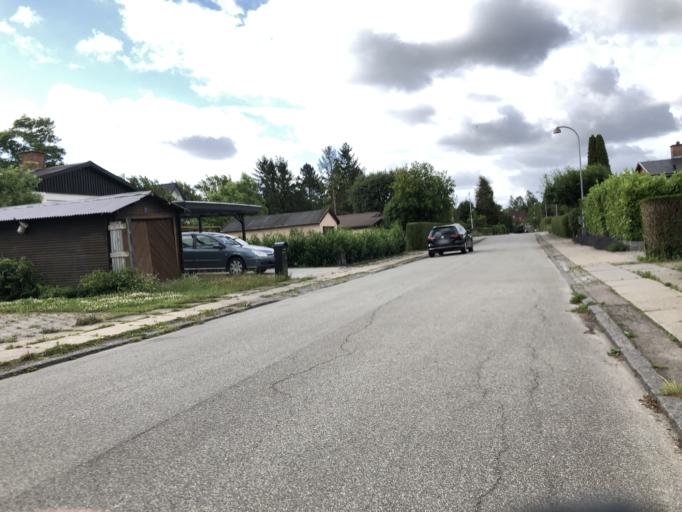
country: DK
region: Capital Region
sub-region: Gladsaxe Municipality
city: Buddinge
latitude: 55.7511
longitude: 12.4858
